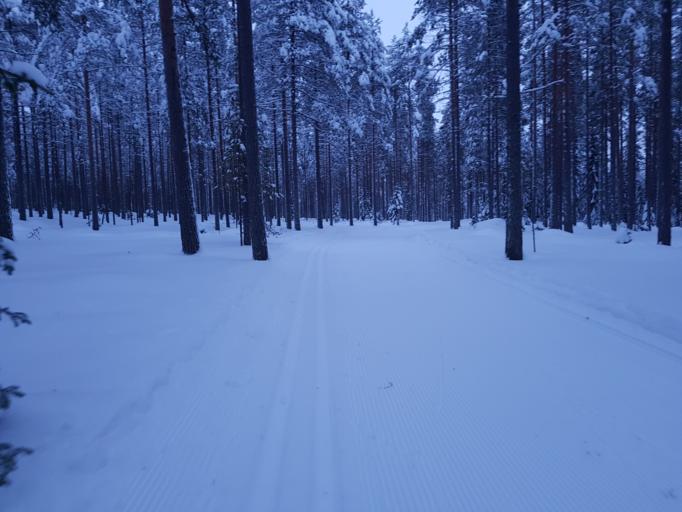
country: FI
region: Kainuu
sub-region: Kehys-Kainuu
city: Kuhmo
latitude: 64.0848
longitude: 29.5198
